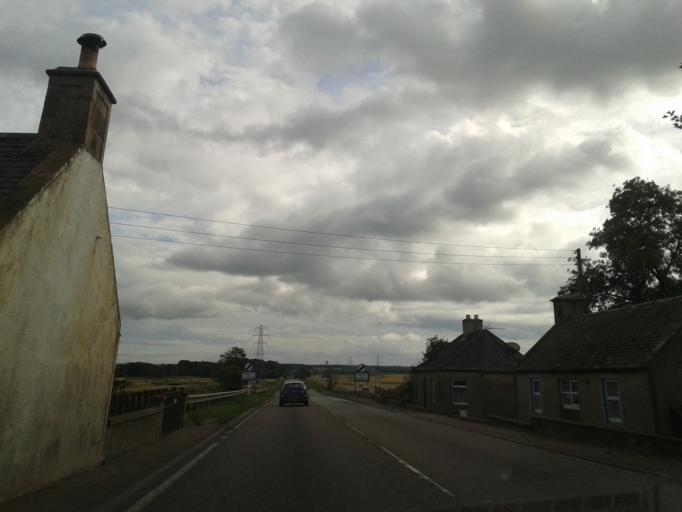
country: GB
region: Scotland
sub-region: Moray
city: Elgin
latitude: 57.6446
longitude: -3.2779
